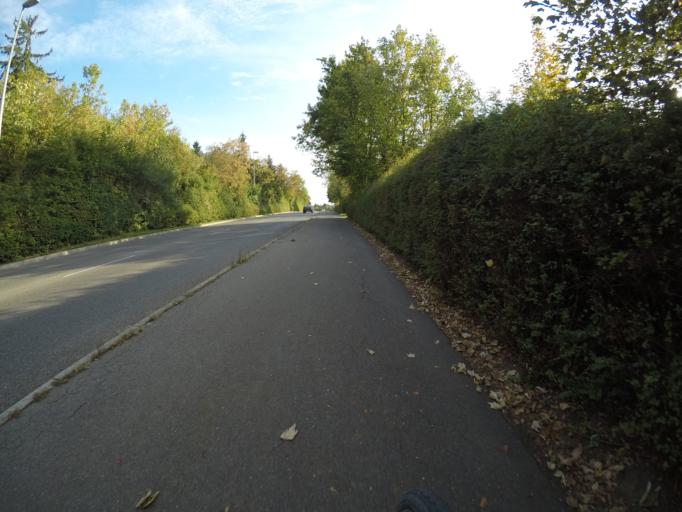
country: DE
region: Baden-Wuerttemberg
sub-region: Tuebingen Region
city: Sickenhausen
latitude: 48.5194
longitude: 9.2009
